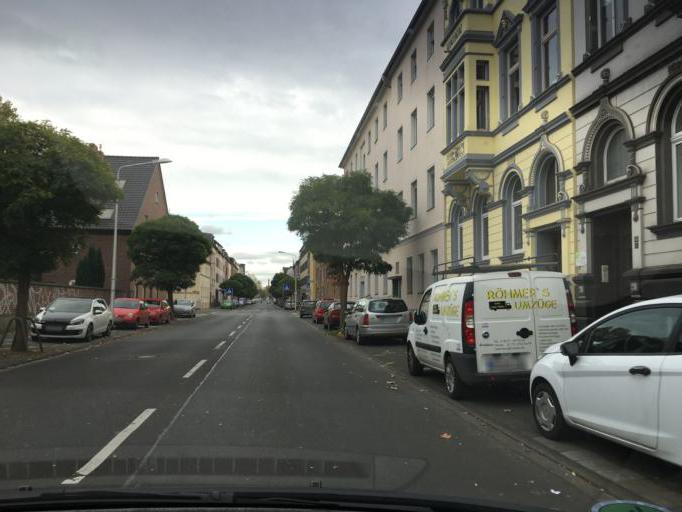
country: DE
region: North Rhine-Westphalia
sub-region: Regierungsbezirk Koln
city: Dueren
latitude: 50.7996
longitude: 6.4730
